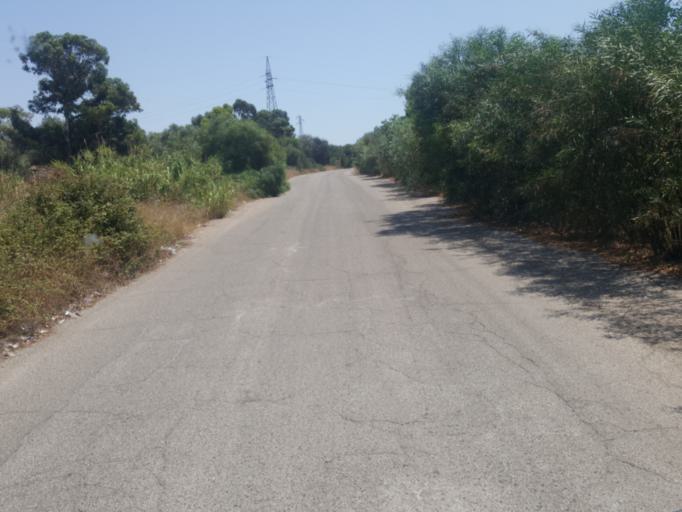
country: IT
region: Apulia
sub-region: Provincia di Taranto
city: Statte
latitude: 40.5041
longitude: 17.1950
